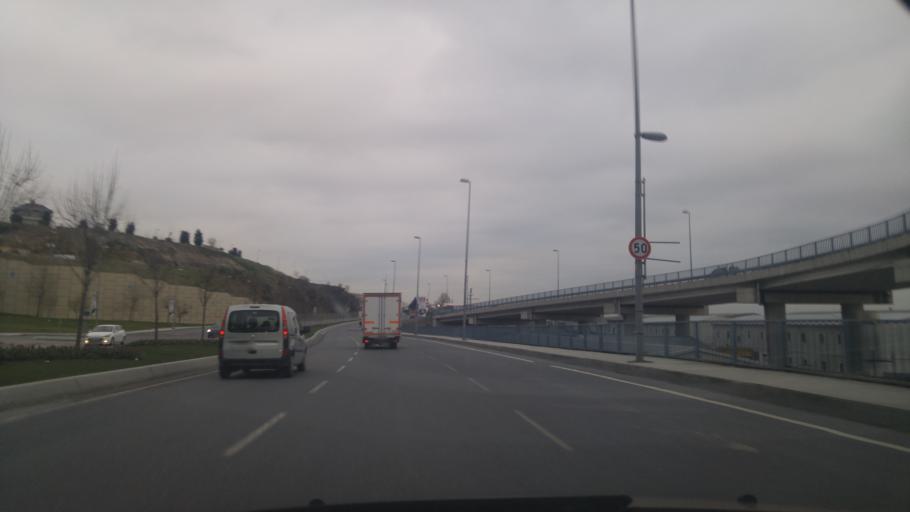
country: TR
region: Istanbul
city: Mahmutbey
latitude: 41.0175
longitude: 28.7683
